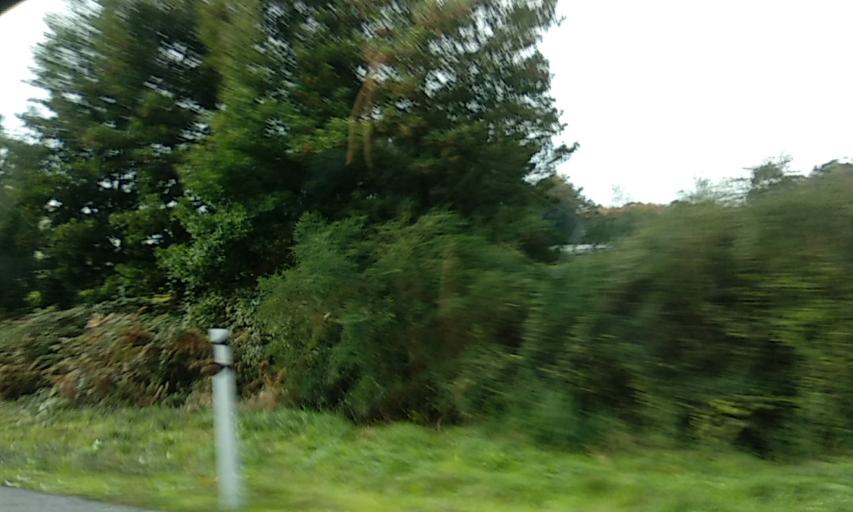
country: PT
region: Braga
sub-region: Vila Nova de Famalicao
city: Vila Nova de Famalicao
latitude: 41.4062
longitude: -8.4936
